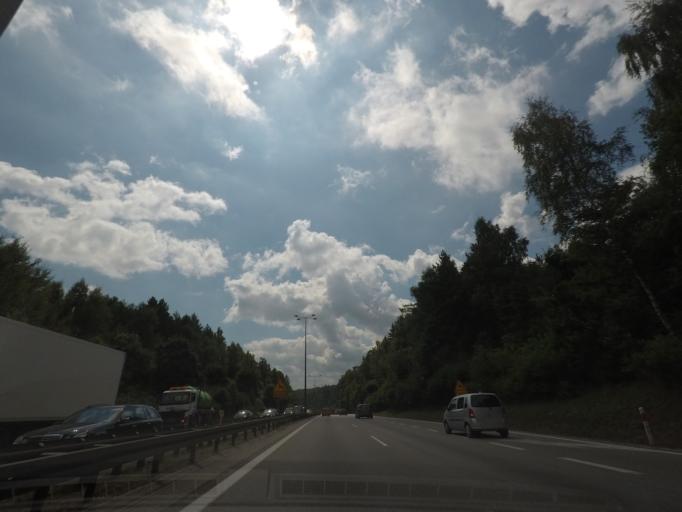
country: PL
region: Pomeranian Voivodeship
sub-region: Gdynia
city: Wielki Kack
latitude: 54.4977
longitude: 18.4619
